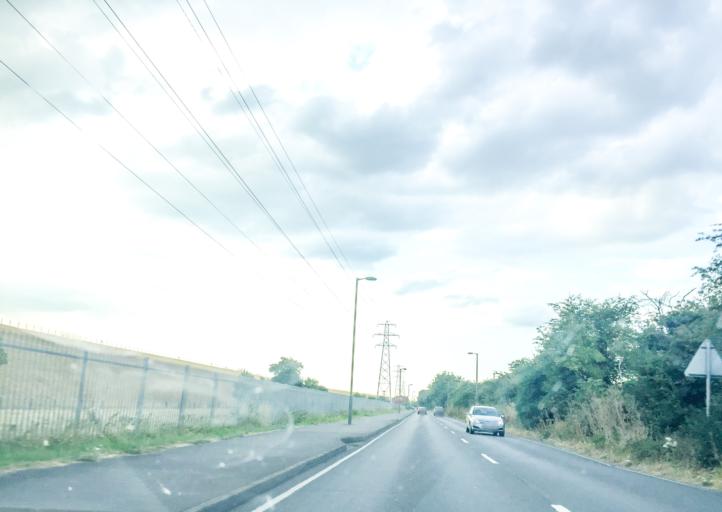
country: GB
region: England
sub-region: Surrey
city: Staines
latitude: 51.4429
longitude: -0.4969
